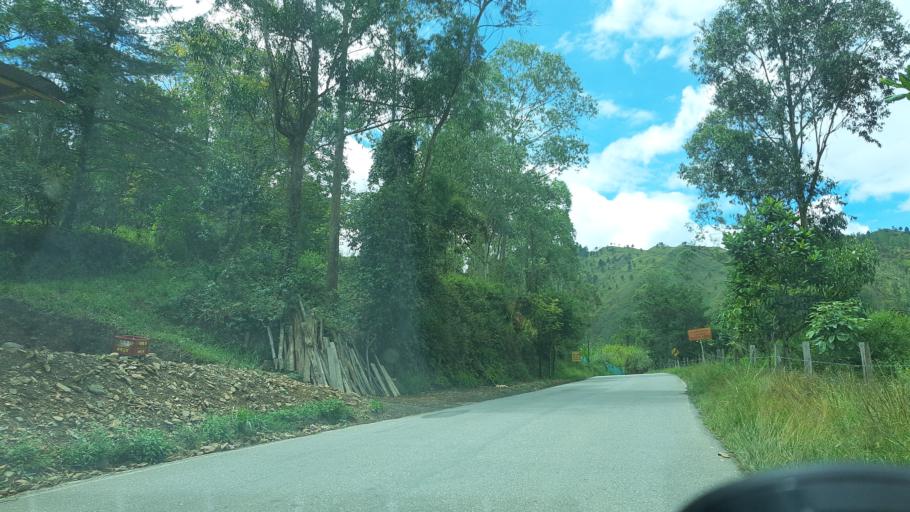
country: CO
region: Cundinamarca
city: Tenza
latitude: 5.0337
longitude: -73.3895
